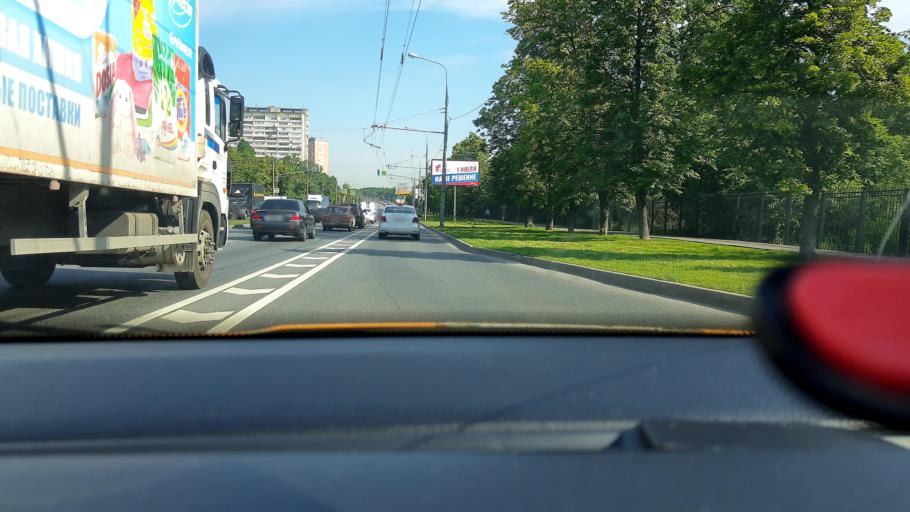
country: RU
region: Moscow
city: Biryulevo
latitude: 55.6006
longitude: 37.6757
